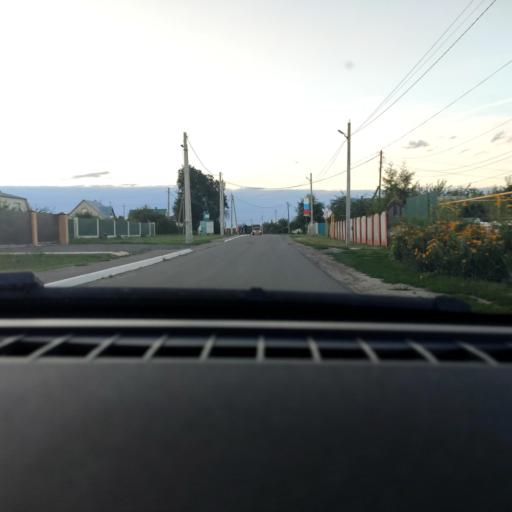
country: RU
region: Voronezj
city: Novaya Usman'
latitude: 51.6626
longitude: 39.3425
